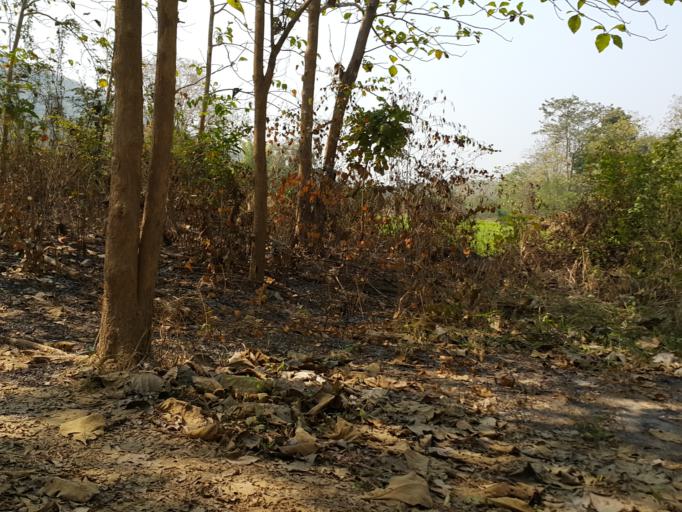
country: TH
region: Sukhothai
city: Thung Saliam
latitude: 17.3289
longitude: 99.4917
